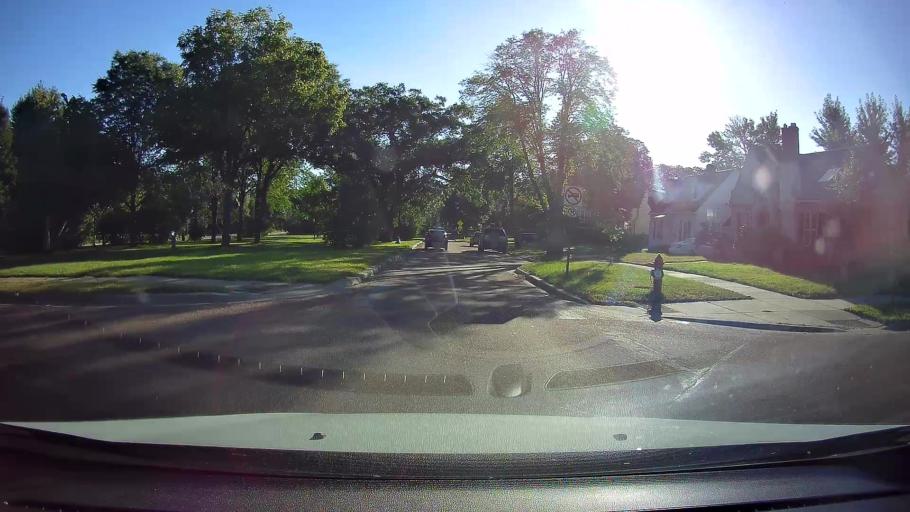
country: US
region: Minnesota
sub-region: Hennepin County
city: Richfield
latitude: 44.9160
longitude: -93.2285
